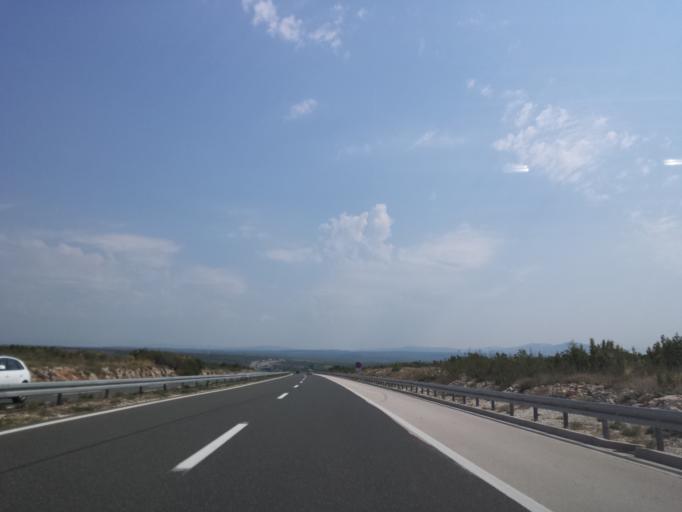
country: HR
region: Sibensko-Kniniska
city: Zaton
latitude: 43.8605
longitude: 15.8279
